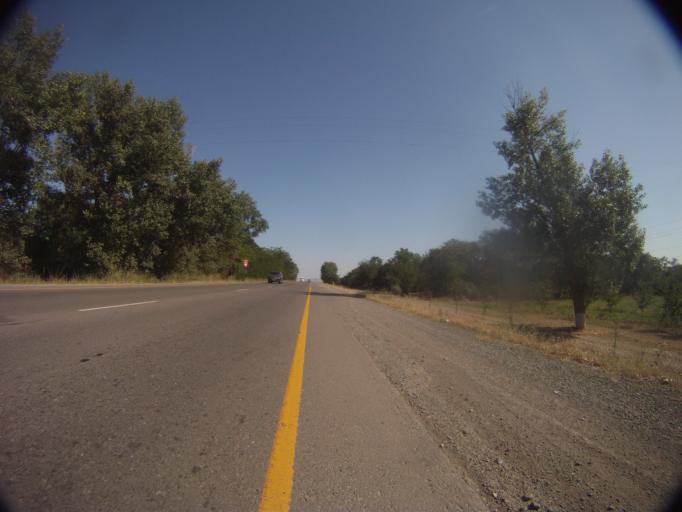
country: AZ
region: Qazax
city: Qazax
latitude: 41.1464
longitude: 45.3189
